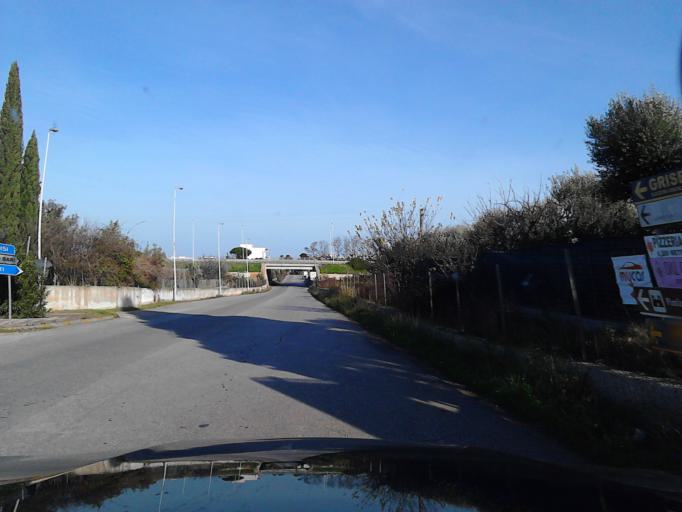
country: IT
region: Apulia
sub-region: Provincia di Bari
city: Mola di Bari
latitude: 41.0497
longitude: 17.0721
